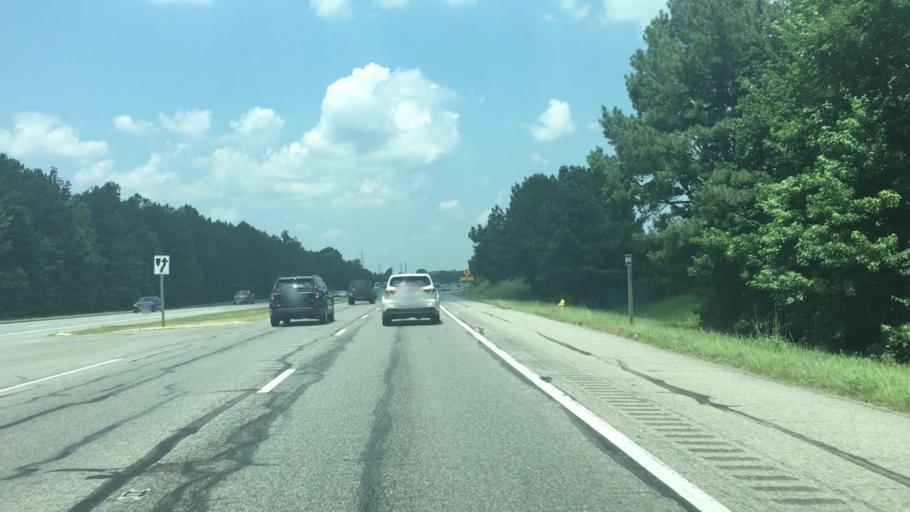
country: US
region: Maryland
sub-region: Saint Mary's County
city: California
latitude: 38.3284
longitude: -76.5525
